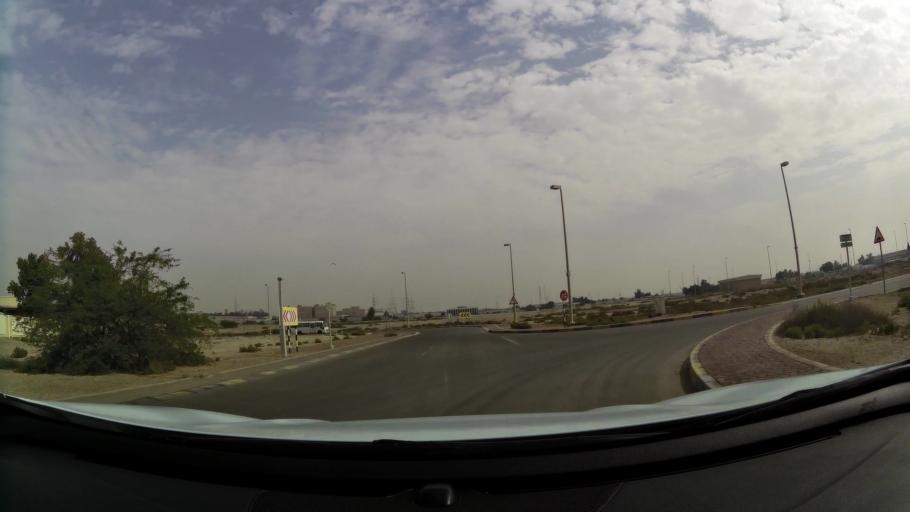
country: AE
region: Abu Dhabi
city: Abu Dhabi
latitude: 24.2875
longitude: 54.6578
